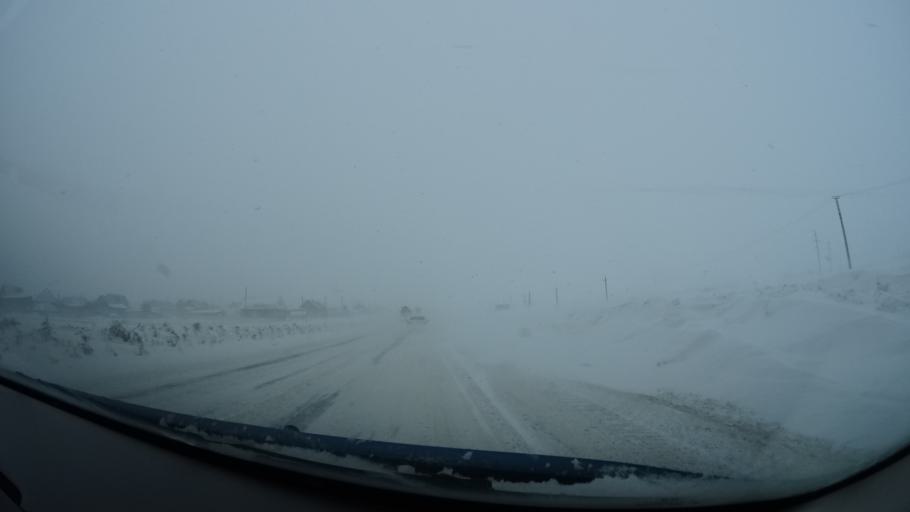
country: RU
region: Perm
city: Kuyeda
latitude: 56.4208
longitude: 55.5855
